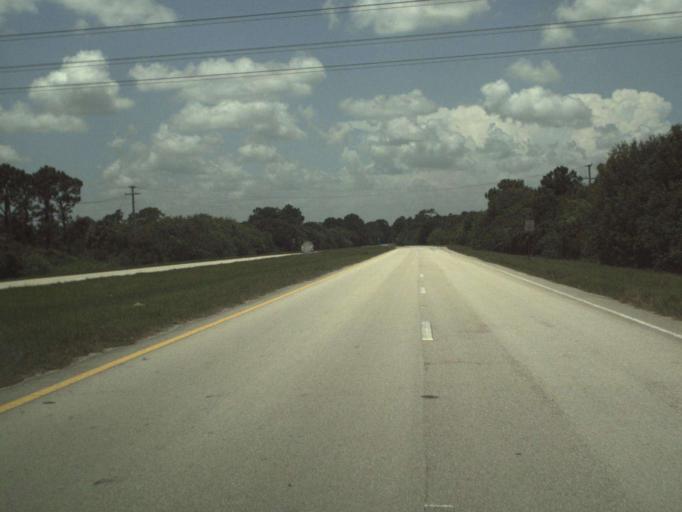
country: US
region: Florida
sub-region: Saint Lucie County
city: Fort Pierce South
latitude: 27.3746
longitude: -80.4165
